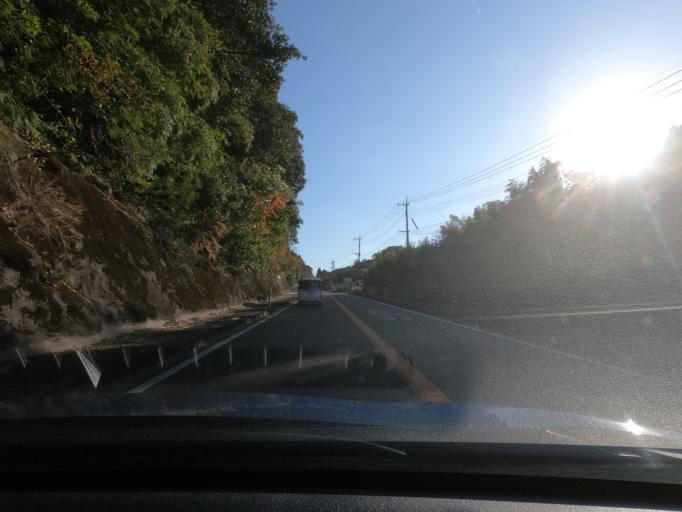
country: JP
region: Kagoshima
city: Akune
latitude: 32.0551
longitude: 130.2213
